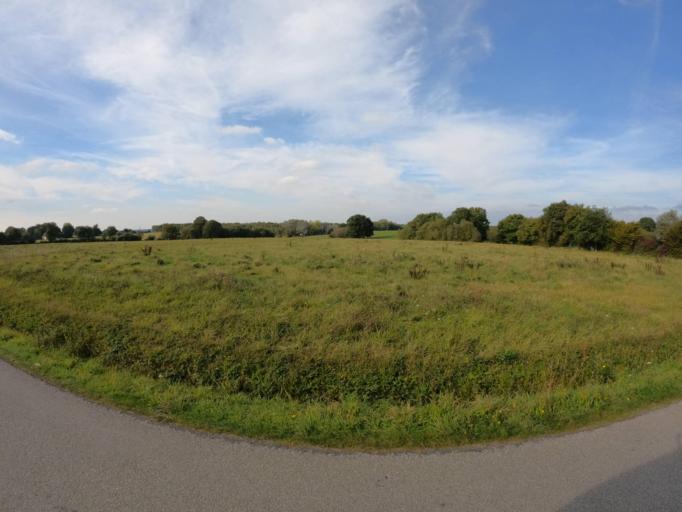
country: FR
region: Brittany
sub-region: Departement du Morbihan
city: Caro
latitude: 47.8865
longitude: -2.3418
